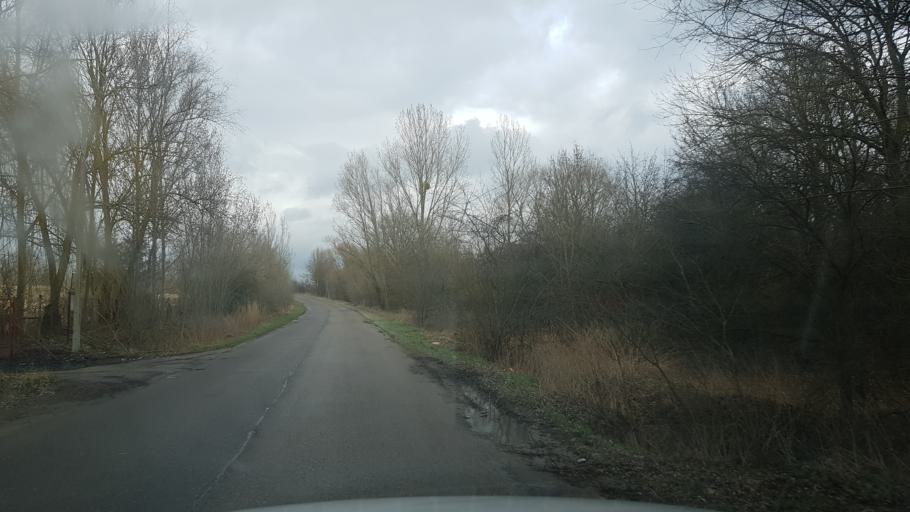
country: PL
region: West Pomeranian Voivodeship
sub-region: Powiat policki
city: Kolbaskowo
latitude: 53.3483
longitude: 14.4390
